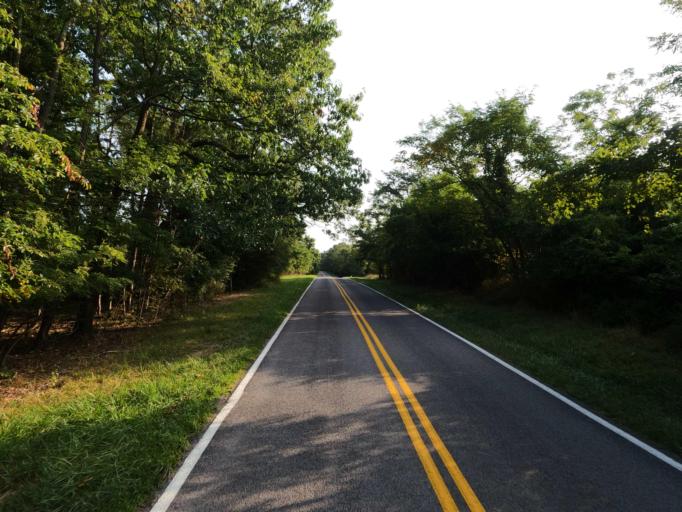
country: US
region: West Virginia
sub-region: Morgan County
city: Berkeley Springs
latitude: 39.6493
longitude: -78.2947
